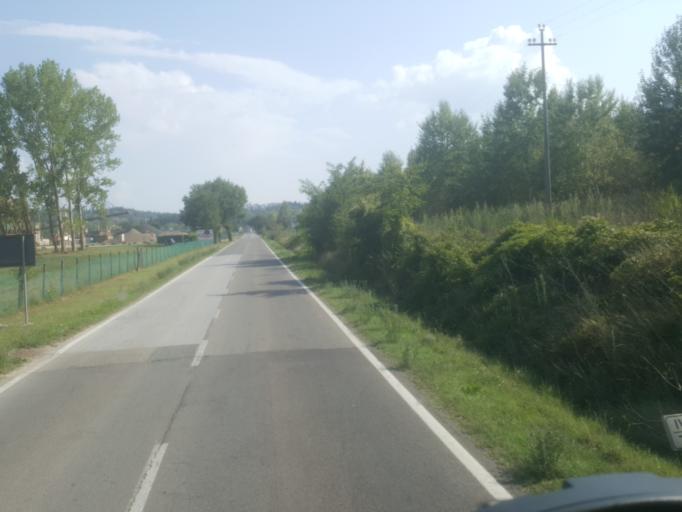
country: IT
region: Tuscany
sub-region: Province of Pisa
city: Lajatico
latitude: 43.5100
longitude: 10.7177
